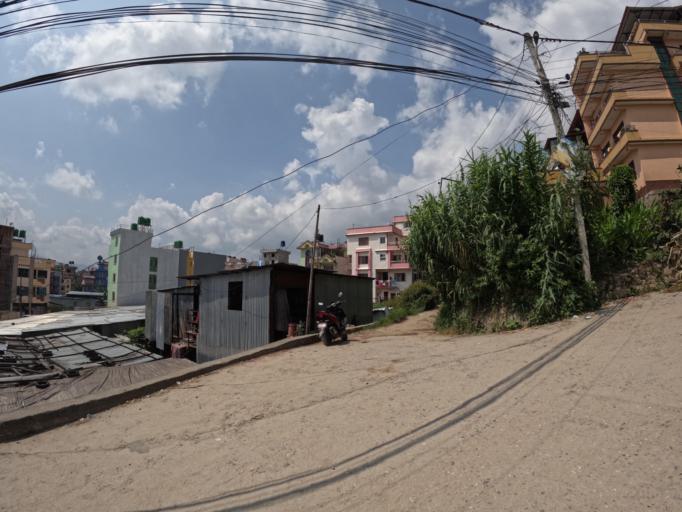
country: NP
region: Central Region
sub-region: Bagmati Zone
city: Patan
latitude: 27.6714
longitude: 85.3590
